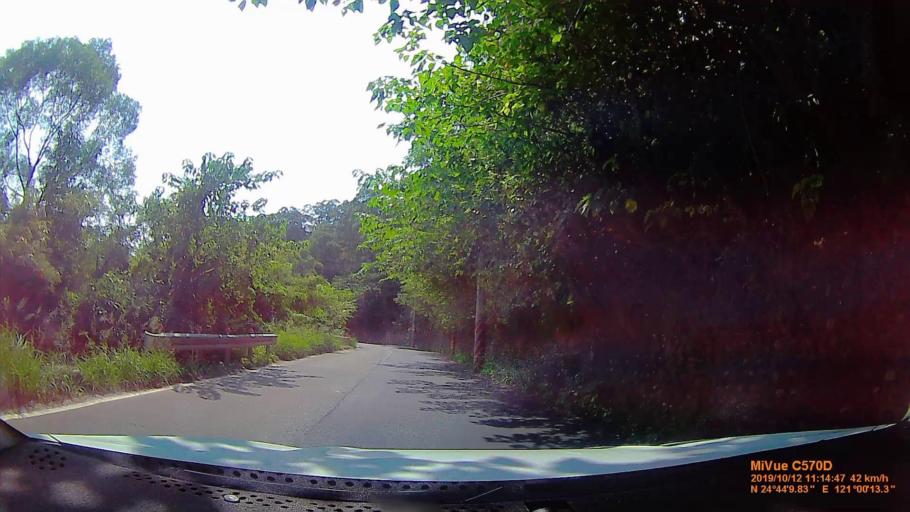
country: TW
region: Taiwan
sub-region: Hsinchu
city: Hsinchu
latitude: 24.7360
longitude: 121.0037
